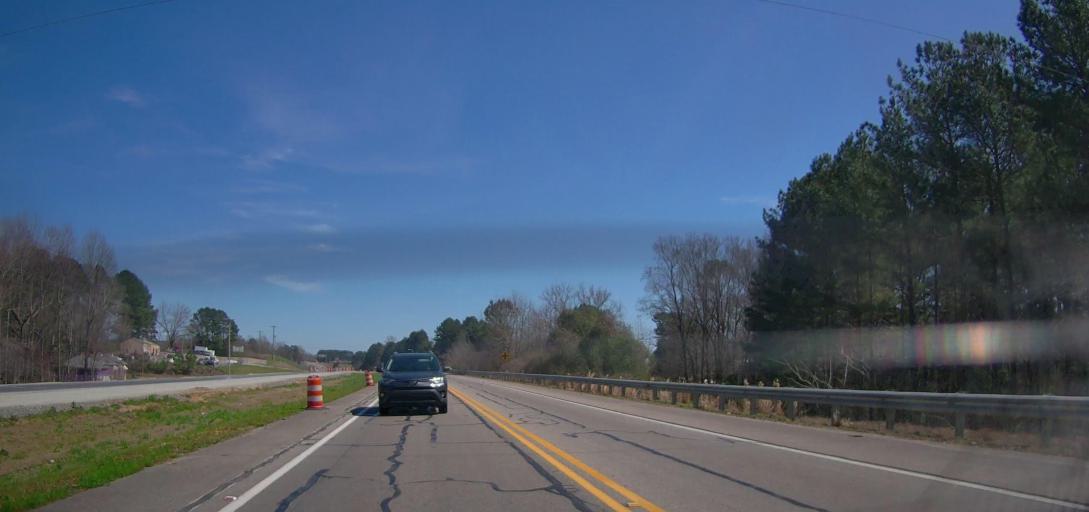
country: US
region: Alabama
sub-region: Cullman County
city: Cullman
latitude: 34.2003
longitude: -86.8199
